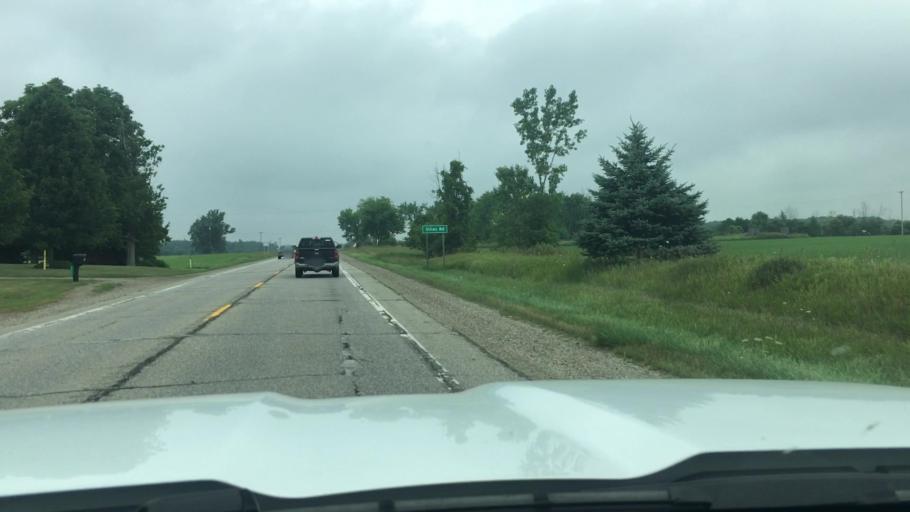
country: US
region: Michigan
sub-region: Sanilac County
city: Marlette
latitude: 43.2381
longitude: -83.0782
